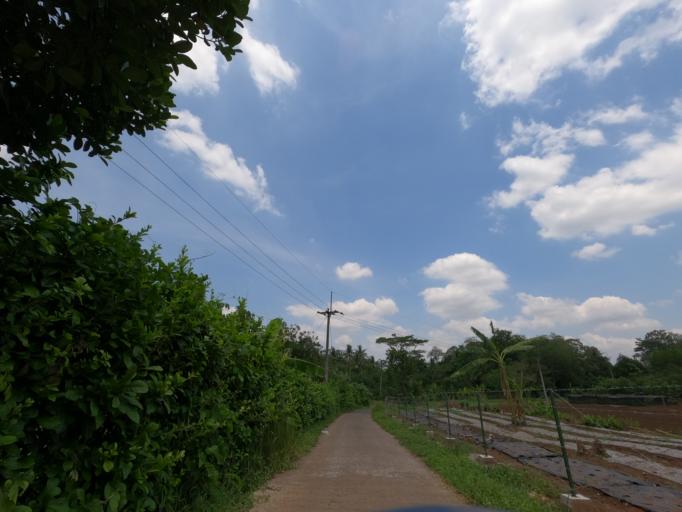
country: ID
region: West Java
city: Pamanukan
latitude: -6.5065
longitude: 107.7711
